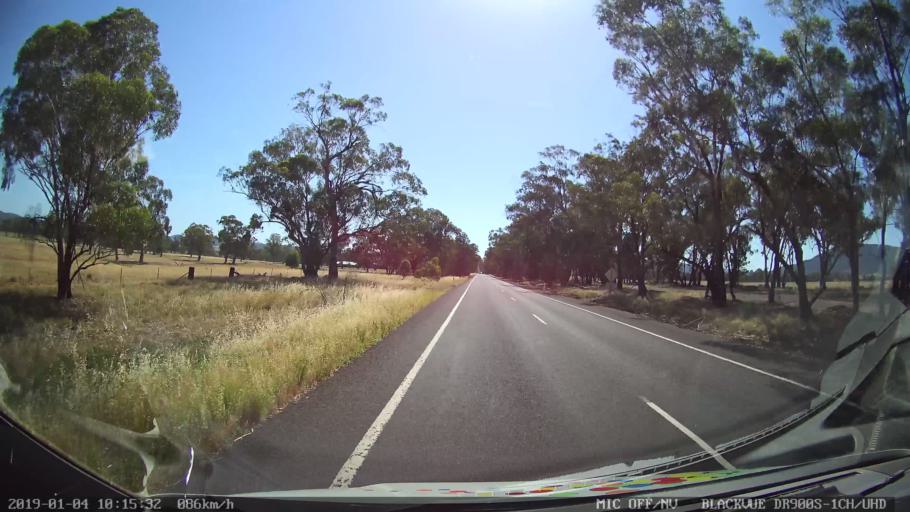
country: AU
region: New South Wales
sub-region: Cabonne
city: Canowindra
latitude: -33.3870
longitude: 148.4229
